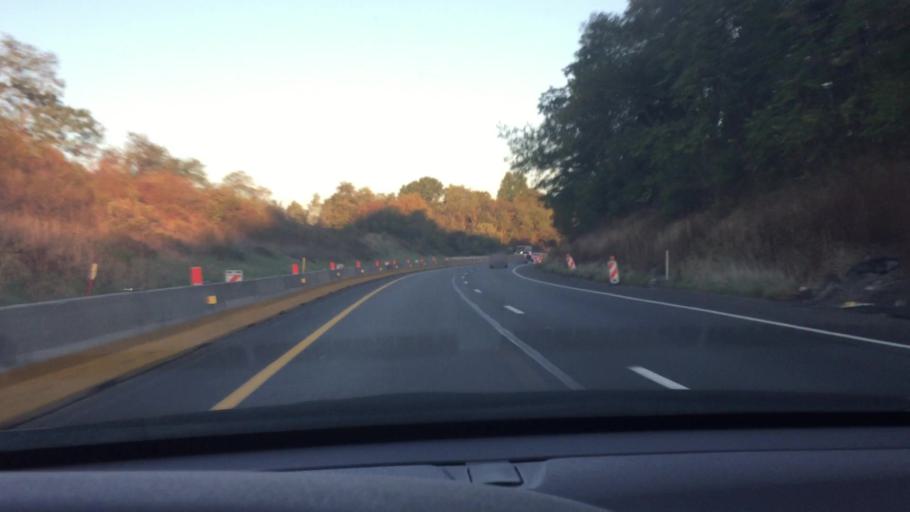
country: US
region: Pennsylvania
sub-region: Washington County
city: East Washington
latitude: 40.1757
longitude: -80.2193
